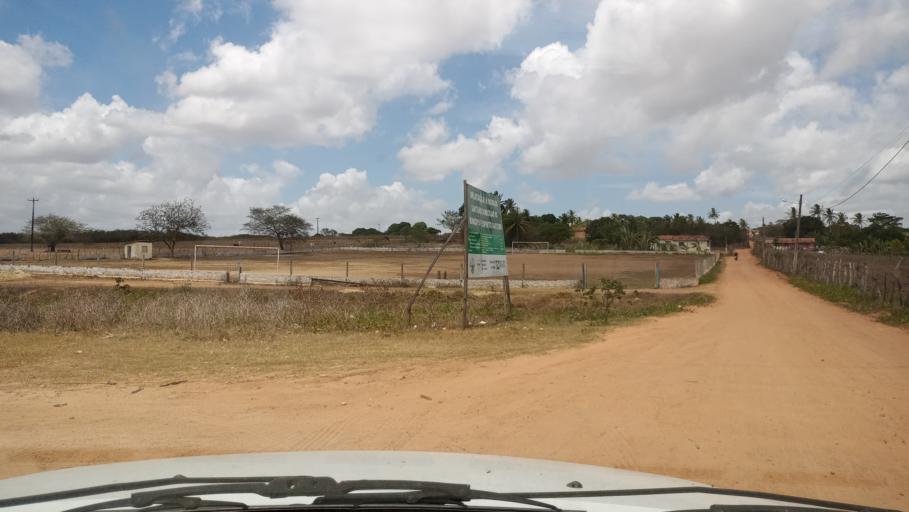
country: BR
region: Rio Grande do Norte
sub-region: Goianinha
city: Goianinha
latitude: -6.2978
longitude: -35.2776
